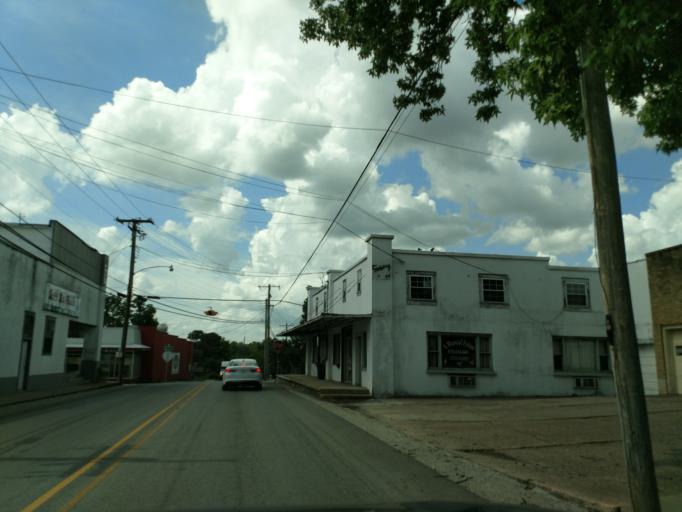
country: US
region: Arkansas
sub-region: Carroll County
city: Berryville
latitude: 36.3651
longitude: -93.5661
